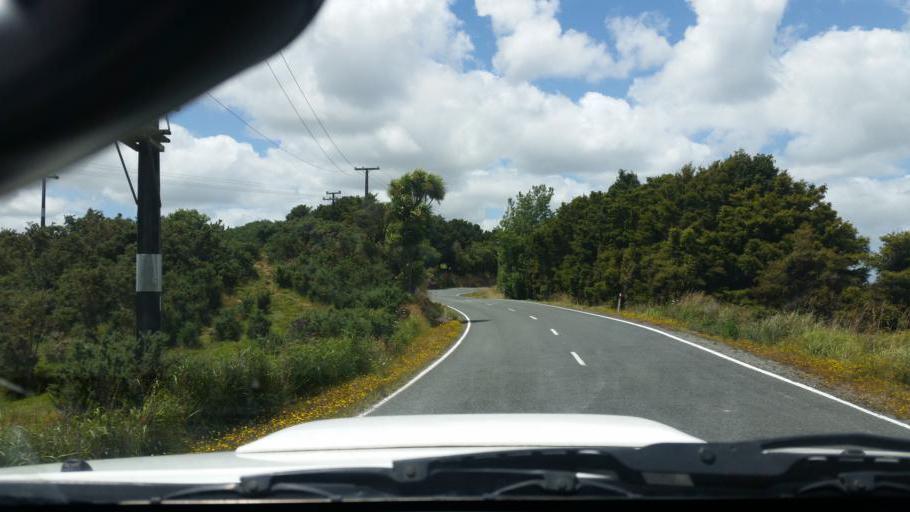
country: NZ
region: Northland
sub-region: Whangarei
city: Ruakaka
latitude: -36.0743
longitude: 174.2600
